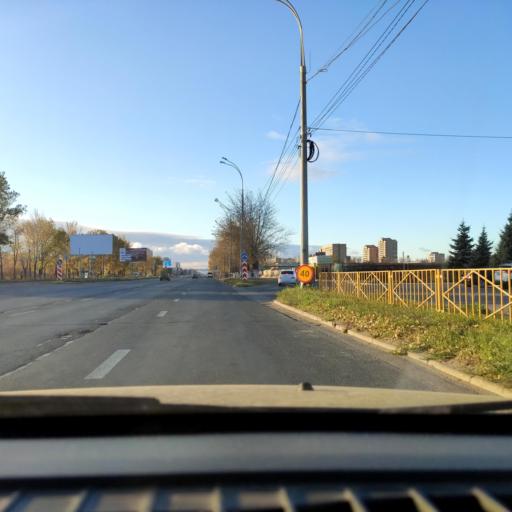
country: RU
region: Samara
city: Tol'yatti
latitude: 53.5427
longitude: 49.2848
